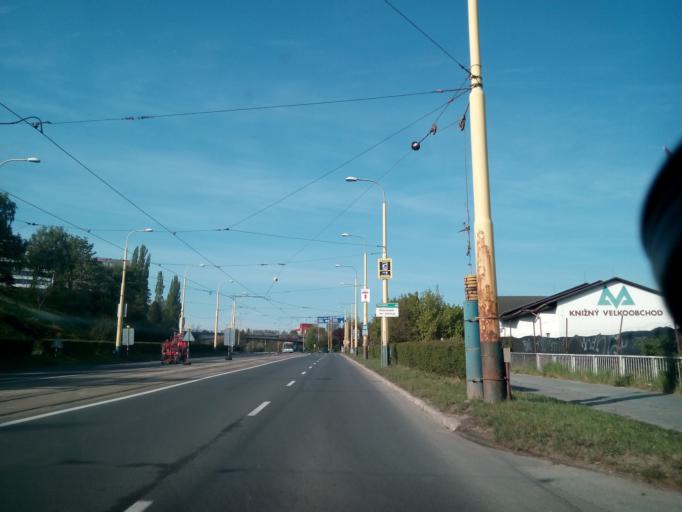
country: SK
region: Kosicky
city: Kosice
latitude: 48.7263
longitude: 21.2389
